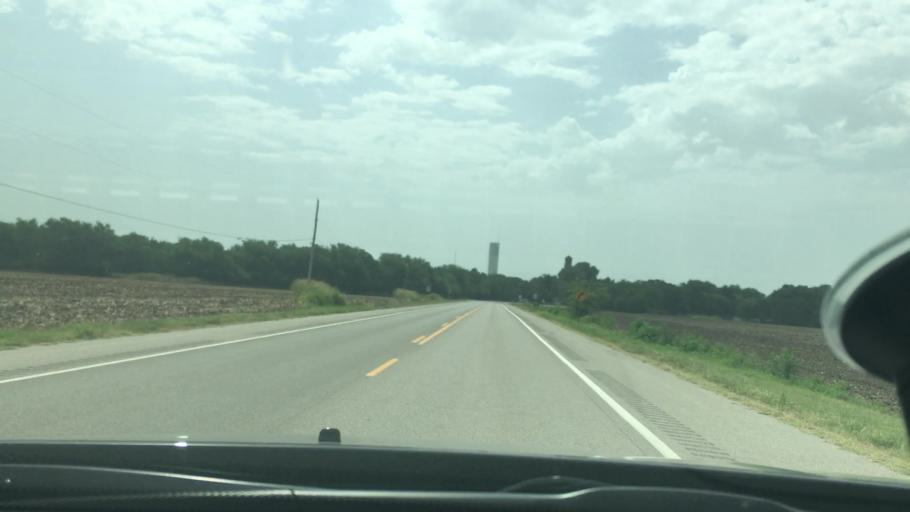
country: US
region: Oklahoma
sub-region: Garvin County
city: Pauls Valley
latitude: 34.8326
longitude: -97.2626
